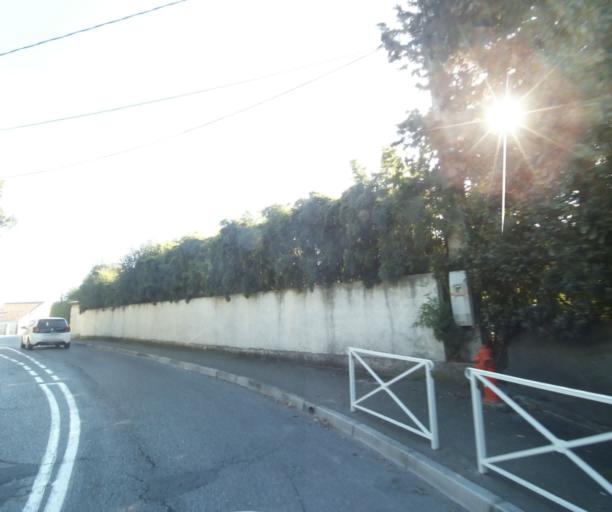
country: FR
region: Provence-Alpes-Cote d'Azur
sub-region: Departement des Alpes-Maritimes
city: Biot
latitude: 43.6029
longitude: 7.1062
